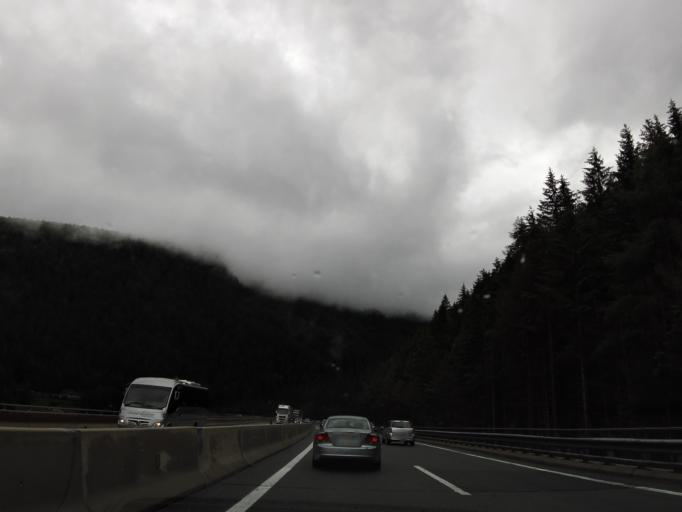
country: AT
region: Tyrol
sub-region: Politischer Bezirk Innsbruck Land
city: Gries am Brenner
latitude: 47.0259
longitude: 11.4950
